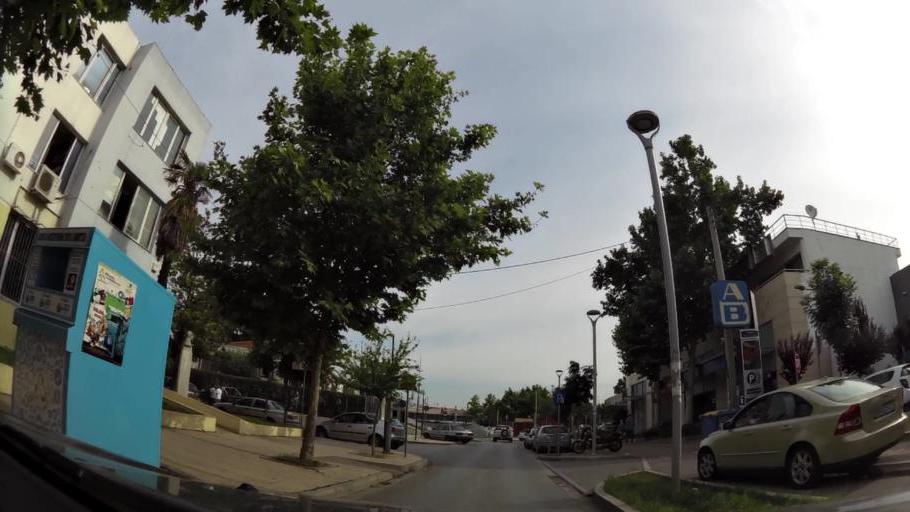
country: GR
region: Central Macedonia
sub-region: Nomos Thessalonikis
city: Thermi
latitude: 40.5462
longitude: 23.0195
